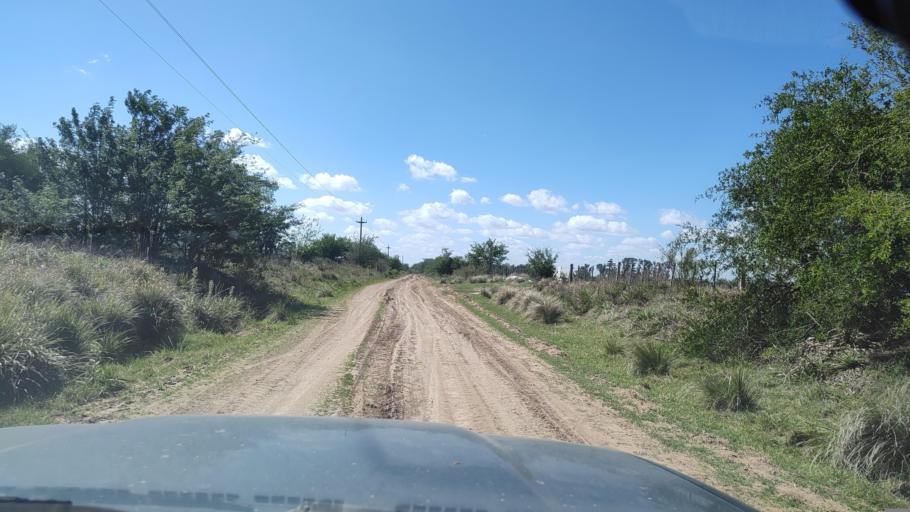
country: AR
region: Buenos Aires
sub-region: Partido de Lujan
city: Lujan
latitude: -34.5243
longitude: -59.1561
